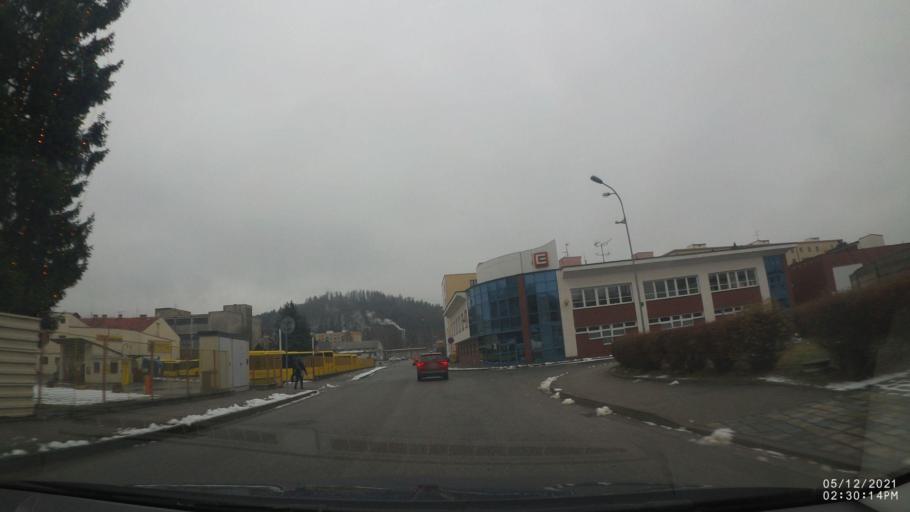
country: CZ
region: Kralovehradecky
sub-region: Okres Nachod
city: Nachod
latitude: 50.4193
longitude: 16.1706
